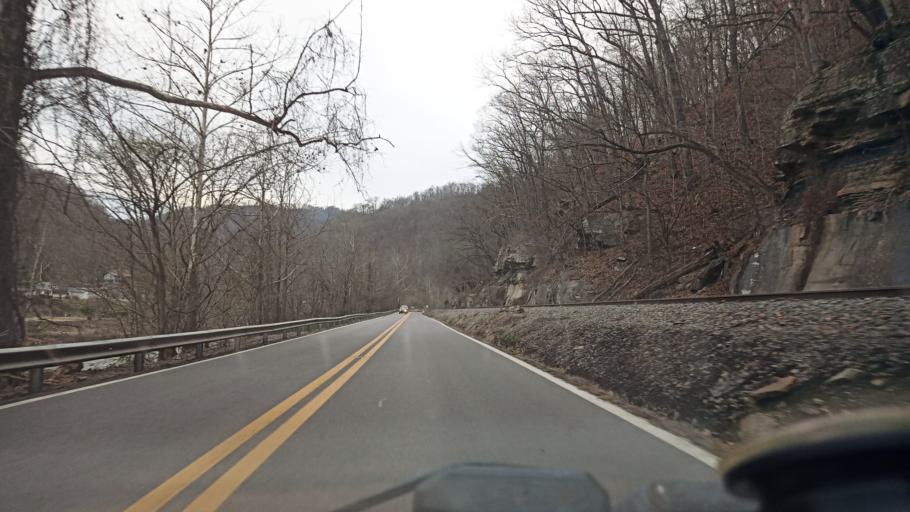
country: US
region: West Virginia
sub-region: Logan County
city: Mallory
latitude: 37.6932
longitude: -81.8623
